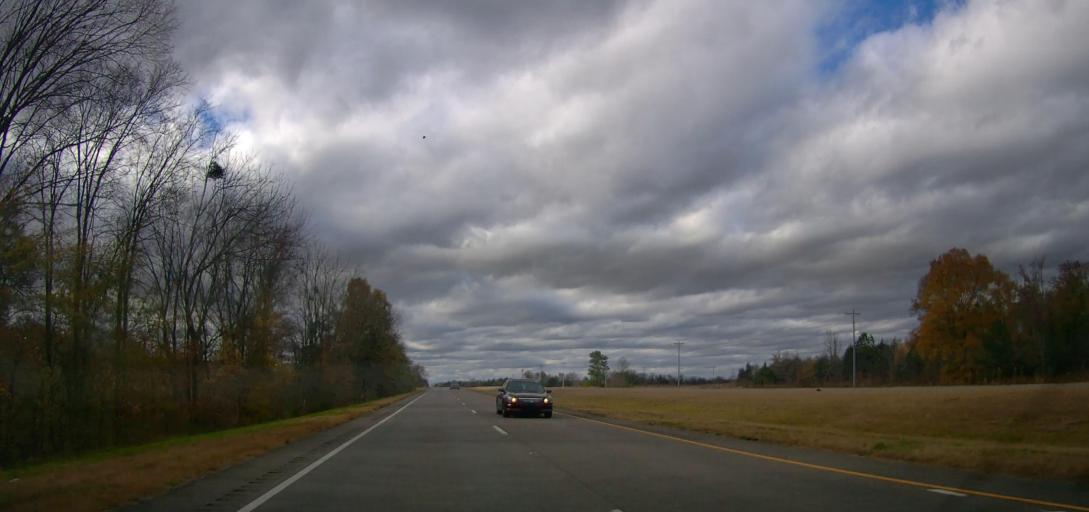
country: US
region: Alabama
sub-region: Morgan County
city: Danville
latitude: 34.3774
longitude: -87.0899
